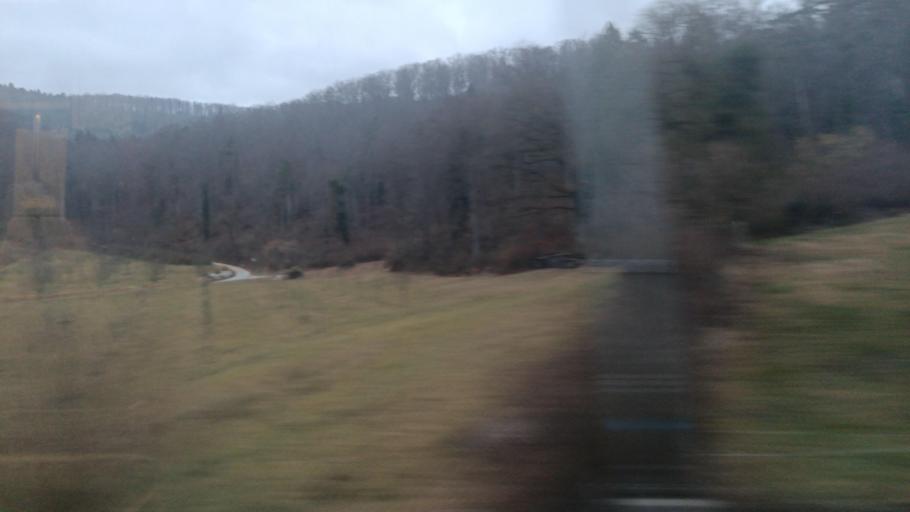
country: CH
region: Aargau
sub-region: Bezirk Brugg
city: Schinznach Dorf
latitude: 47.4573
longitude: 8.1367
